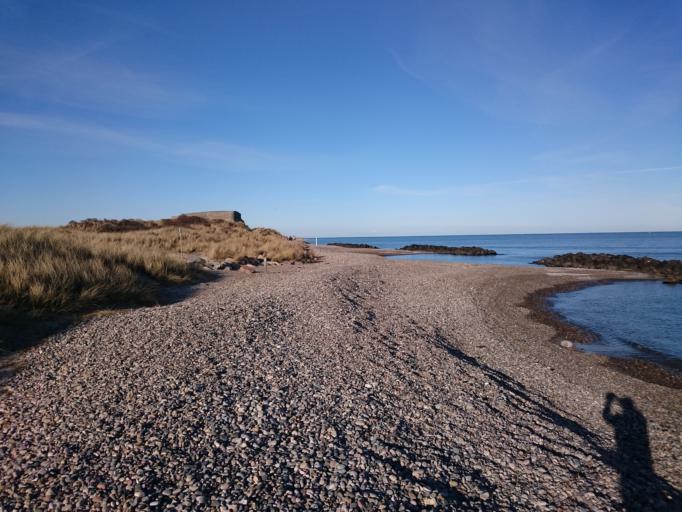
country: DK
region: North Denmark
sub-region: Frederikshavn Kommune
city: Skagen
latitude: 57.7383
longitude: 10.6367
